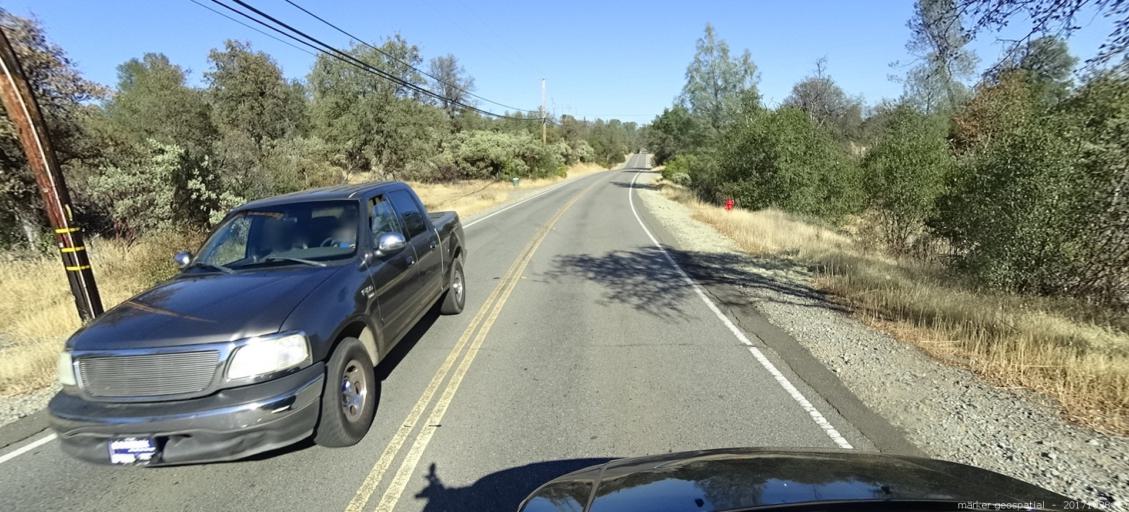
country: US
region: California
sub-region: Shasta County
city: Redding
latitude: 40.6205
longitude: -122.4261
